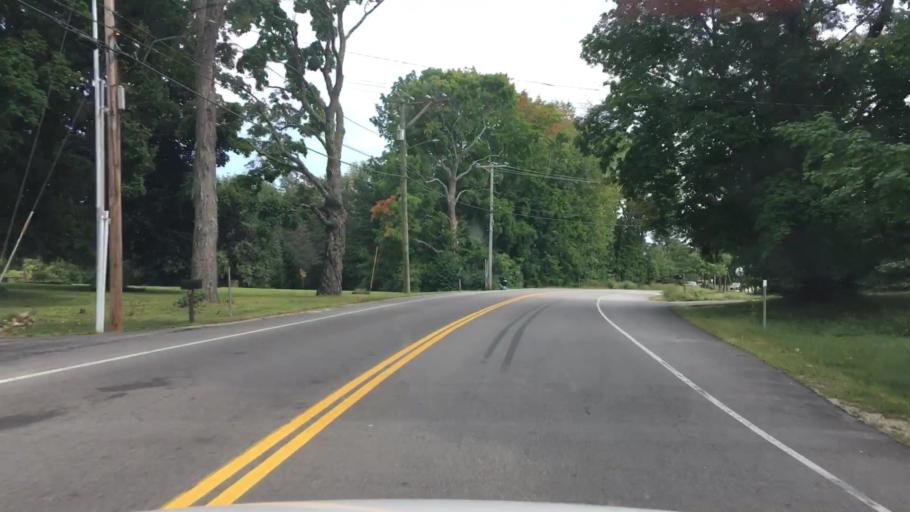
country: US
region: New Hampshire
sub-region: Strafford County
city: Dover
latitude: 43.1892
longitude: -70.9012
